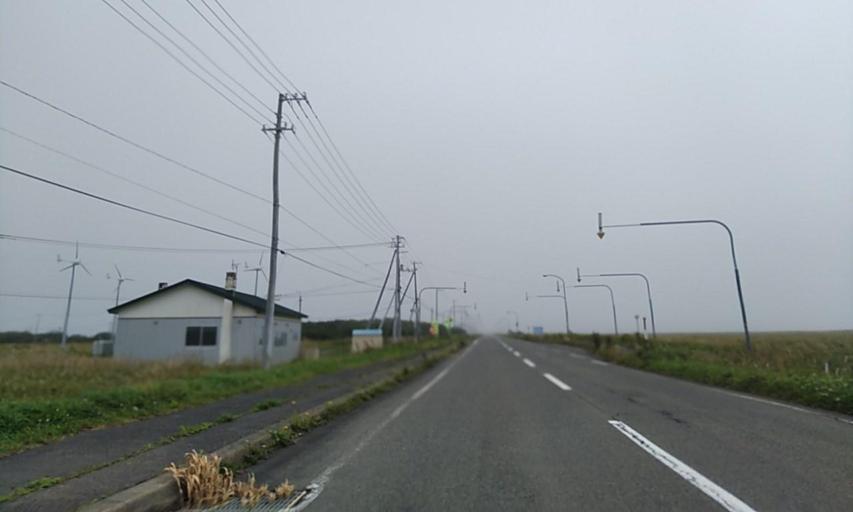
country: JP
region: Hokkaido
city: Nemuro
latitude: 43.3892
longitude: 145.7567
